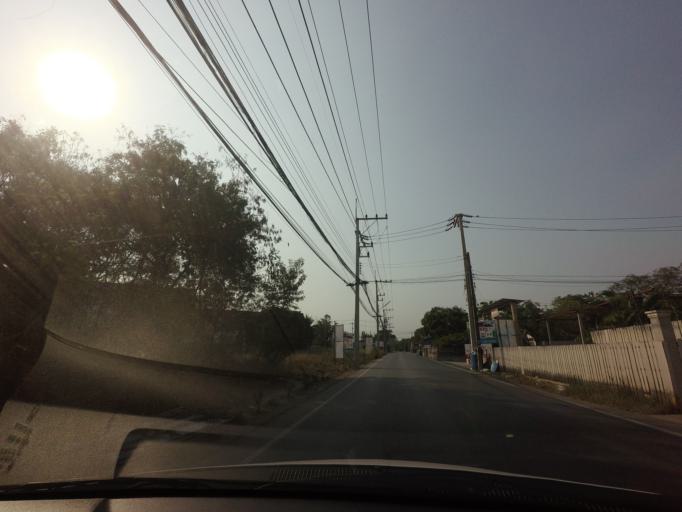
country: TH
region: Samut Sakhon
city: Krathum Baen
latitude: 13.6937
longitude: 100.2523
